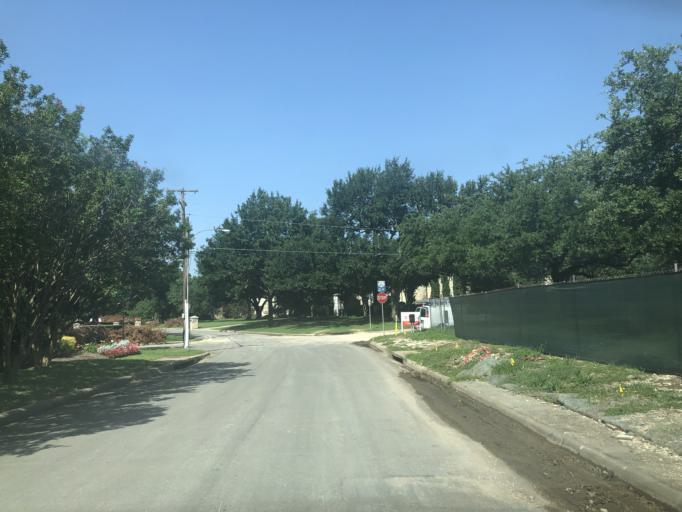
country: US
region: Texas
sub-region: Dallas County
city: University Park
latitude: 32.8842
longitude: -96.8162
